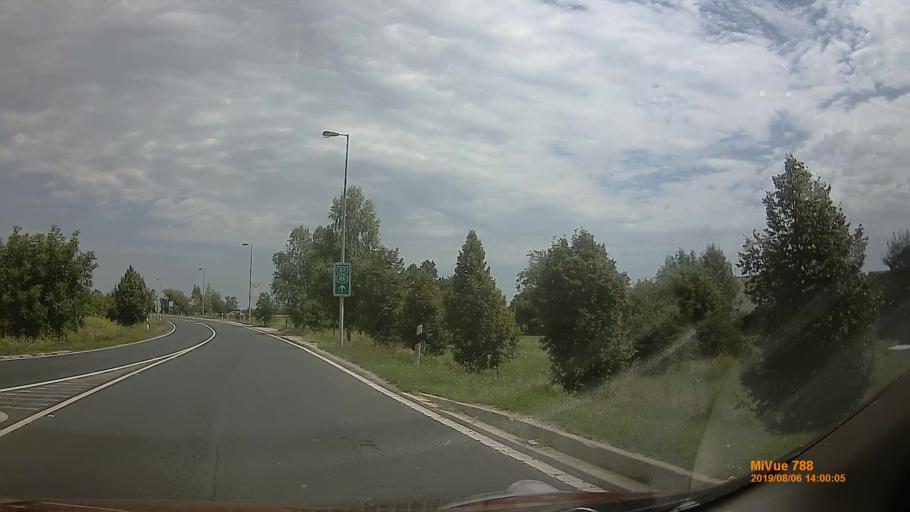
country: HU
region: Vas
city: Gencsapati
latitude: 47.2644
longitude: 16.6039
